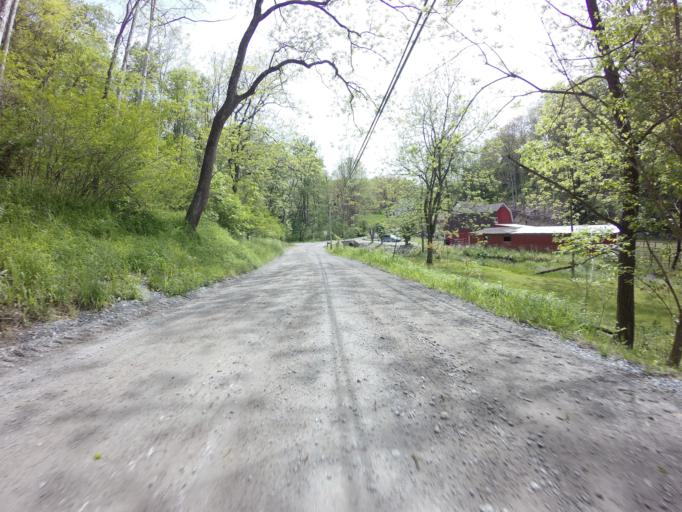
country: US
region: Maryland
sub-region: Carroll County
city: New Windsor
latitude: 39.4941
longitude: -77.1072
